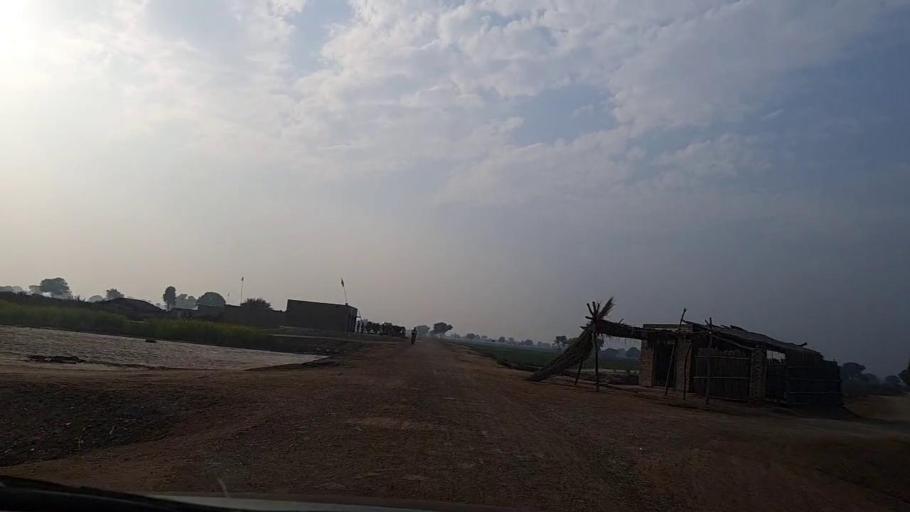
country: PK
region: Sindh
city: Nawabshah
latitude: 26.2739
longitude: 68.3322
